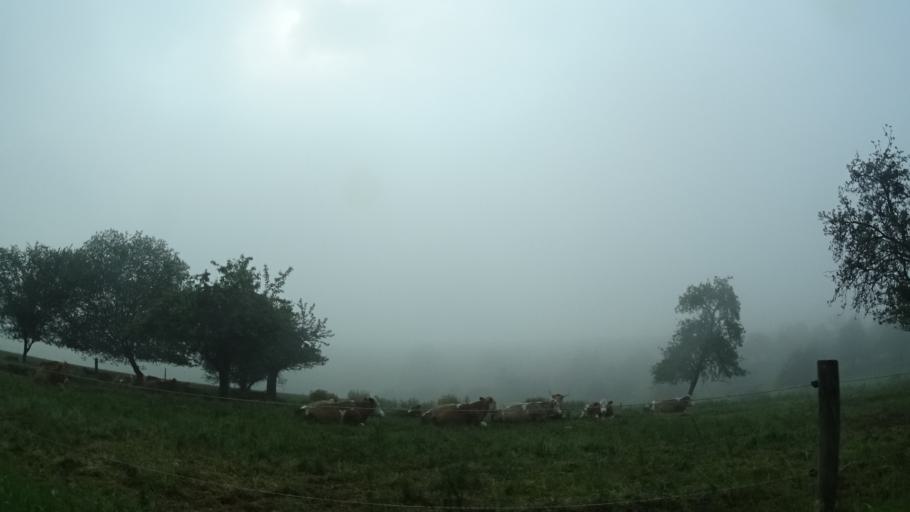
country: DE
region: Bavaria
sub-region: Regierungsbezirk Unterfranken
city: Eschau
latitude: 49.8123
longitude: 9.2343
